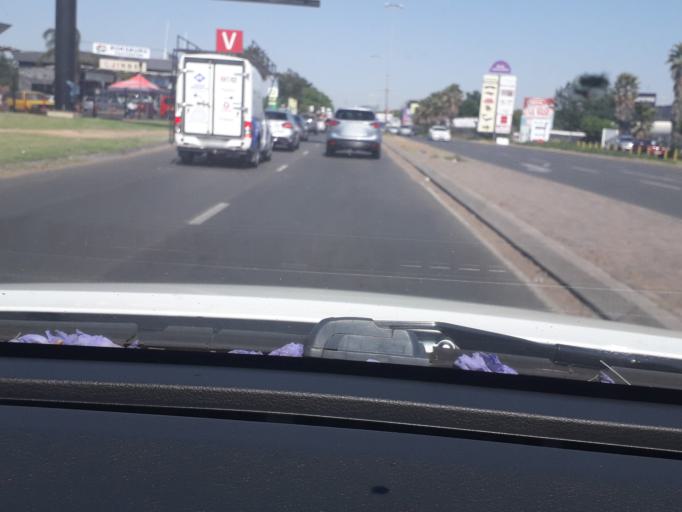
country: ZA
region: Gauteng
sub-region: Ekurhuleni Metropolitan Municipality
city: Boksburg
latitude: -26.1793
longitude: 28.2802
